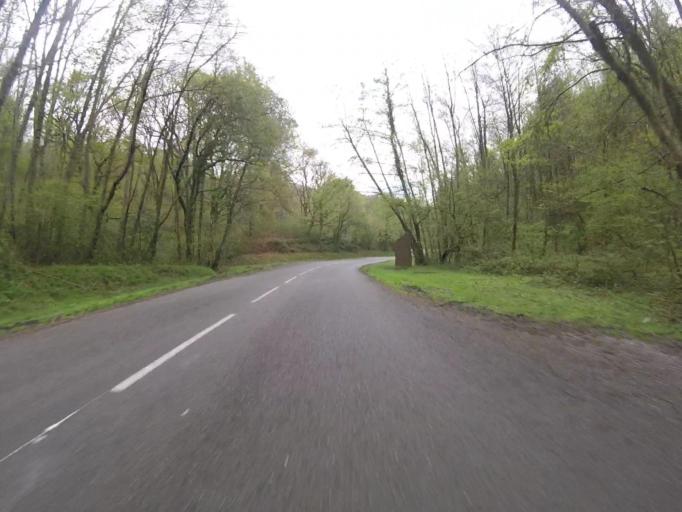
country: ES
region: Navarre
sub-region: Provincia de Navarra
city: Etxalar
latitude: 43.2826
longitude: -1.6290
